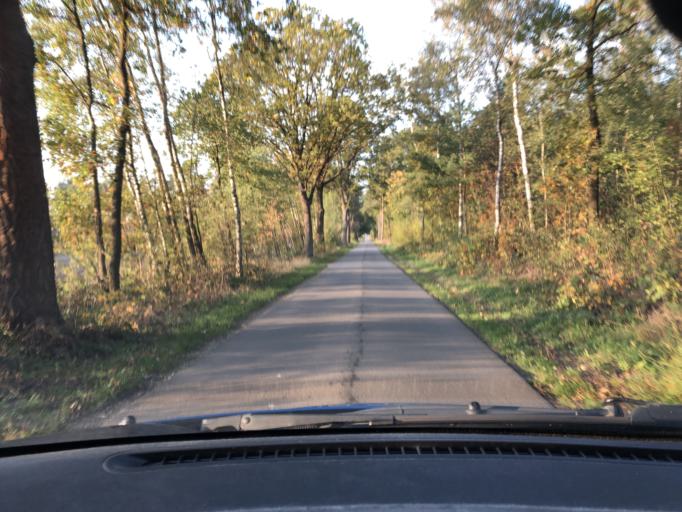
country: DE
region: Lower Saxony
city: Hitzacker
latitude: 53.1319
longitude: 11.0093
